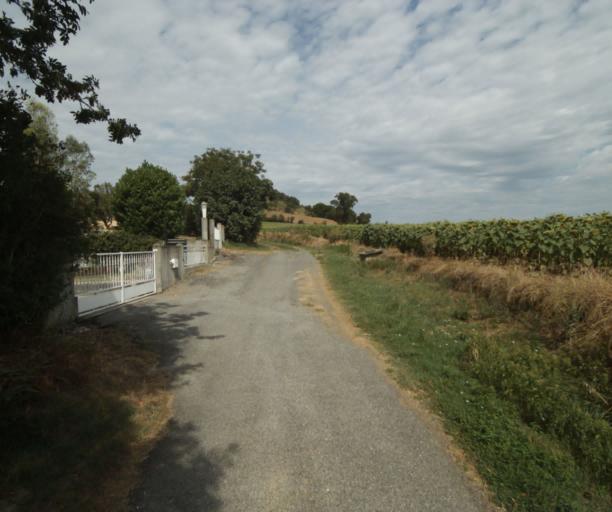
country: FR
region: Midi-Pyrenees
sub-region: Departement de la Haute-Garonne
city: Saint-Felix-Lauragais
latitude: 43.4437
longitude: 1.9058
